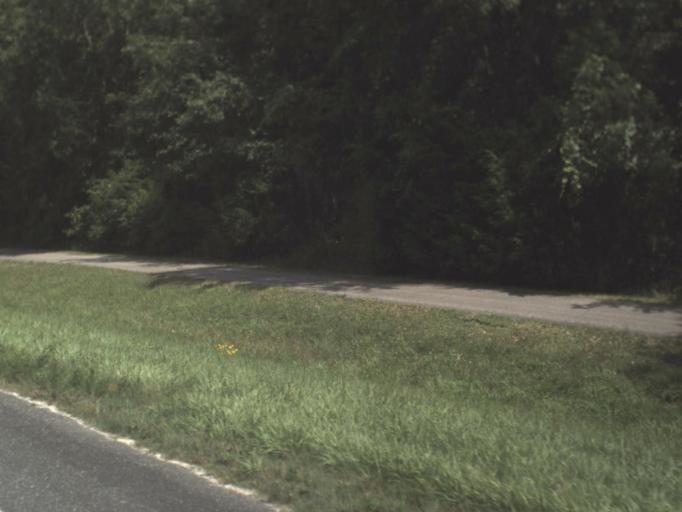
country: US
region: Florida
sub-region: Suwannee County
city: Wellborn
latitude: 29.9524
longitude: -82.8855
